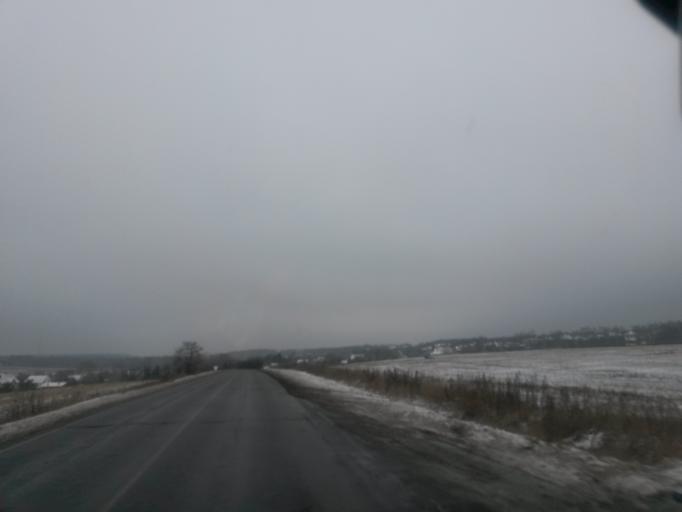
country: RU
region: Moskovskaya
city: Lyubuchany
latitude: 55.2619
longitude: 37.6077
